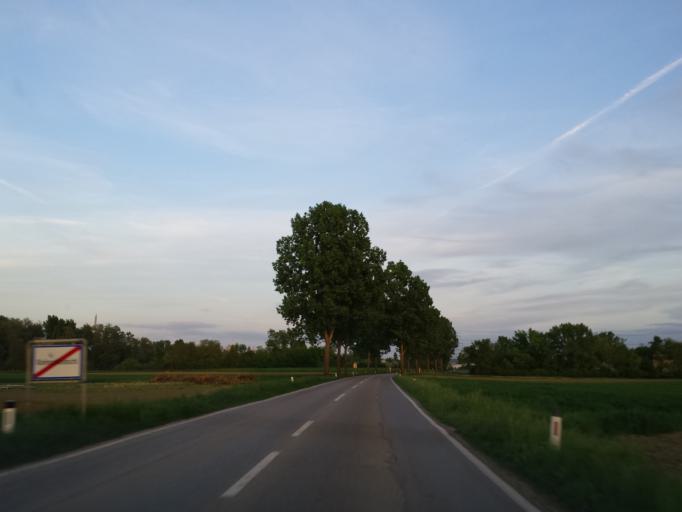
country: AT
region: Lower Austria
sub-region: Politischer Bezirk Tulln
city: Michelhausen
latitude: 48.3381
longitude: 15.9368
